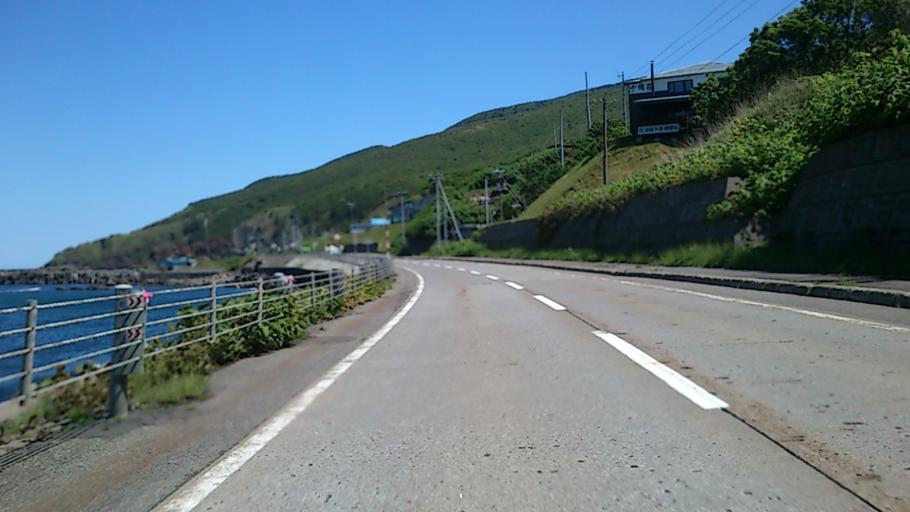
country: JP
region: Hokkaido
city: Rumoi
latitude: 43.7722
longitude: 141.3672
